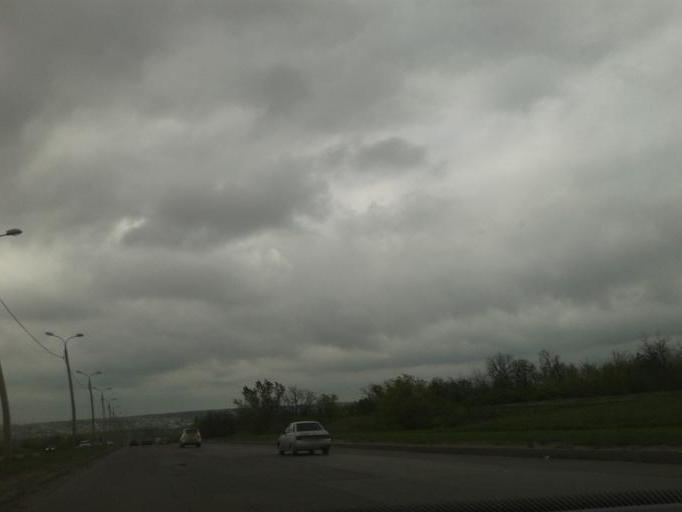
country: RU
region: Volgograd
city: Volgograd
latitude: 48.7416
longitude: 44.4624
